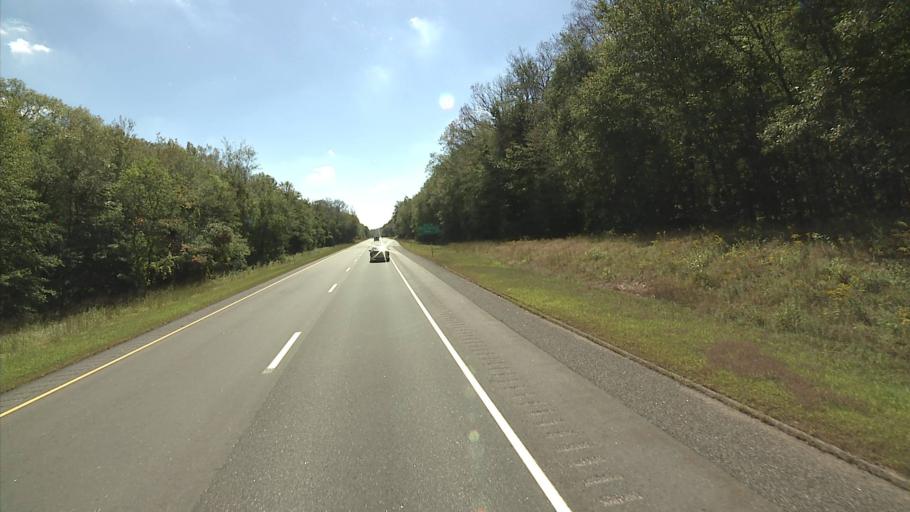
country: US
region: Connecticut
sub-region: New London County
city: Colchester
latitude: 41.5093
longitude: -72.3027
